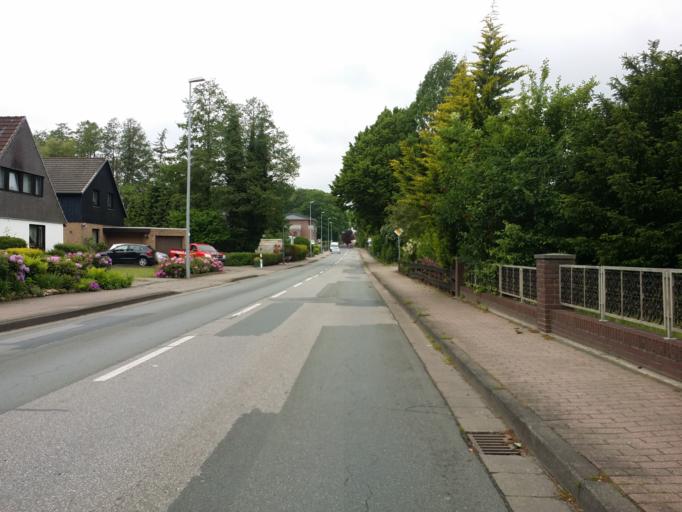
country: DE
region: Lower Saxony
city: Ganderkesee
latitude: 53.0301
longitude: 8.5614
